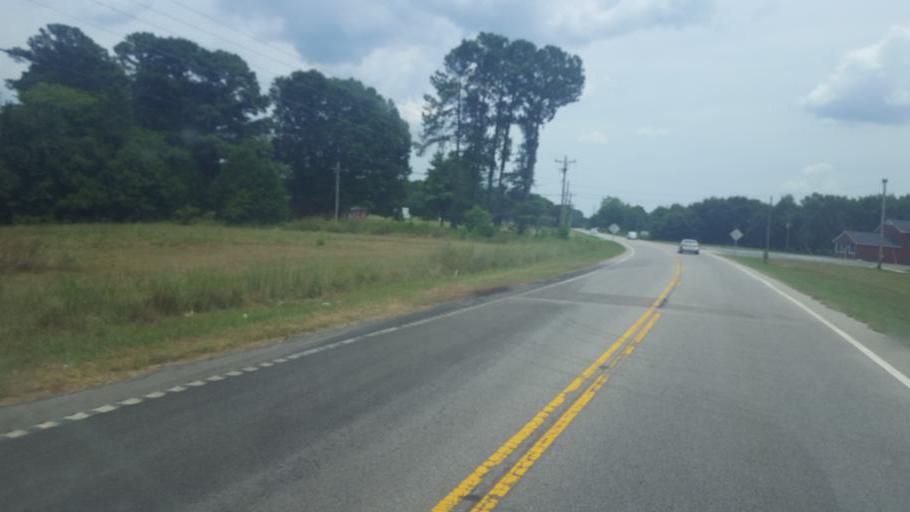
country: US
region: South Carolina
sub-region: York County
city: Newport
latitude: 34.9641
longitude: -81.1477
